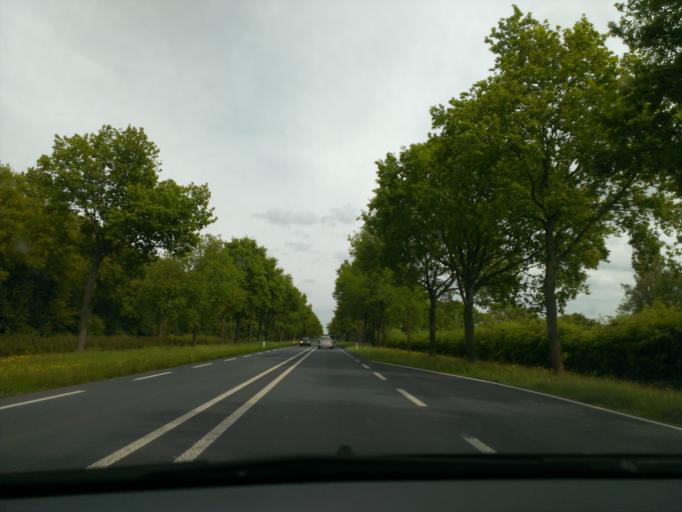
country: NL
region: Gelderland
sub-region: Gemeente Epe
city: Epe
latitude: 52.3368
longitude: 5.9874
